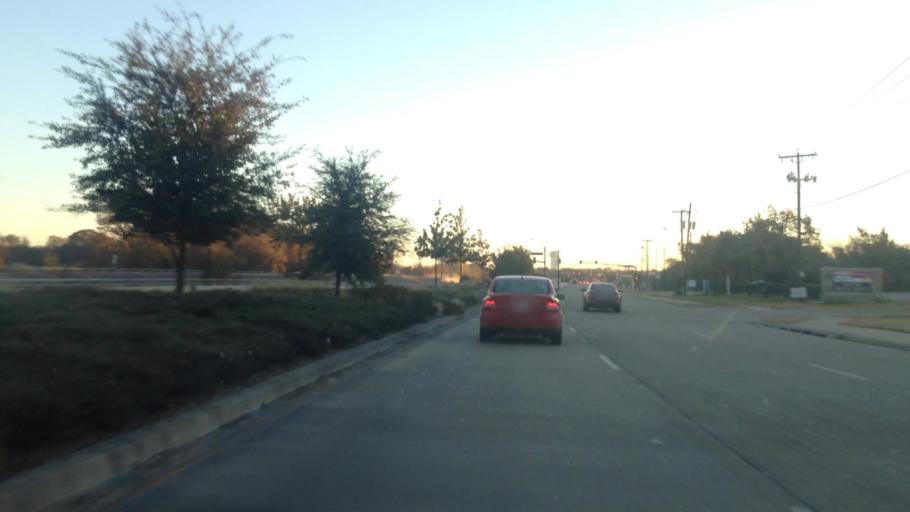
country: US
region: Texas
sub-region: Tarrant County
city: Southlake
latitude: 32.9124
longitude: -97.1328
